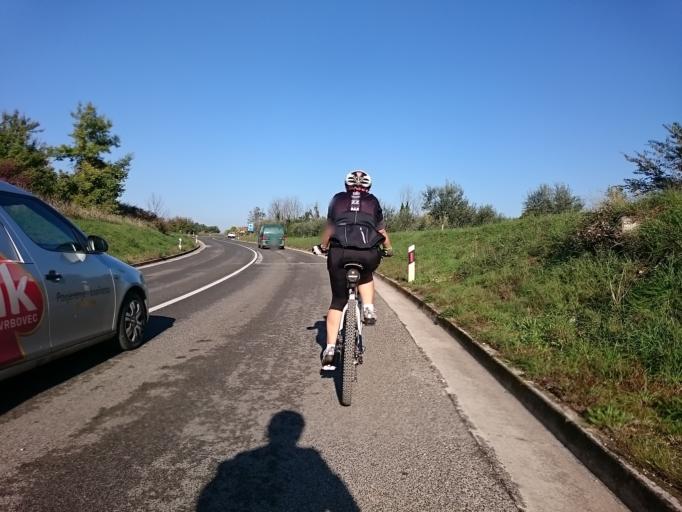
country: HR
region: Istarska
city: Buje
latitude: 45.3745
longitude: 13.6231
